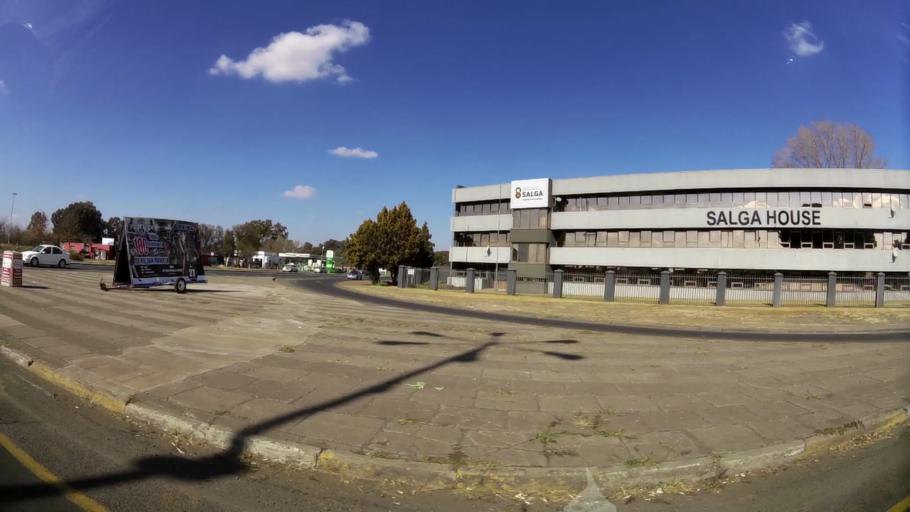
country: ZA
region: Orange Free State
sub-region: Mangaung Metropolitan Municipality
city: Bloemfontein
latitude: -29.1180
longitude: 26.2364
